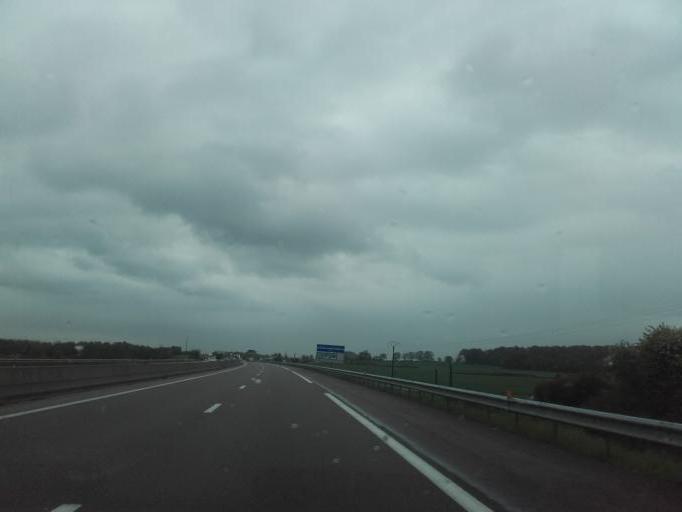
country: FR
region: Bourgogne
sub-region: Departement de l'Yonne
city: Avallon
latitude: 47.5036
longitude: 4.0255
